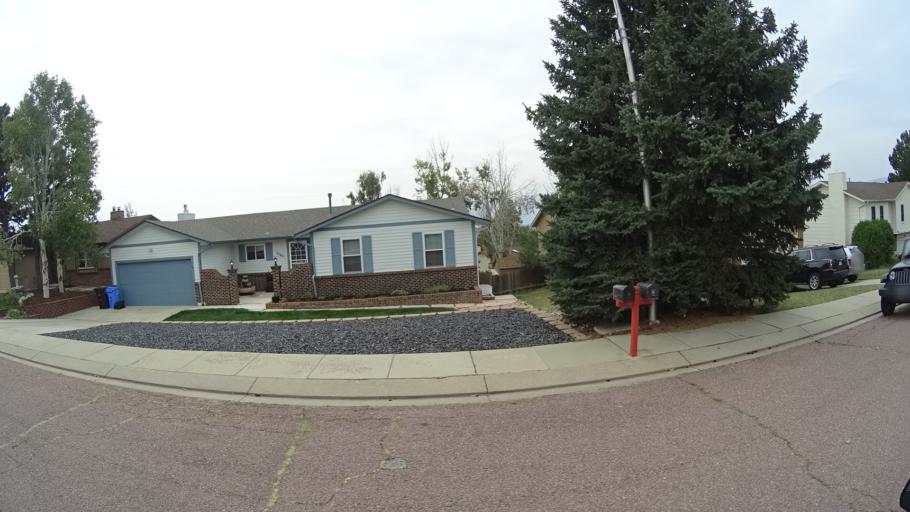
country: US
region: Colorado
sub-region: El Paso County
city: Cimarron Hills
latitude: 38.9046
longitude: -104.7315
